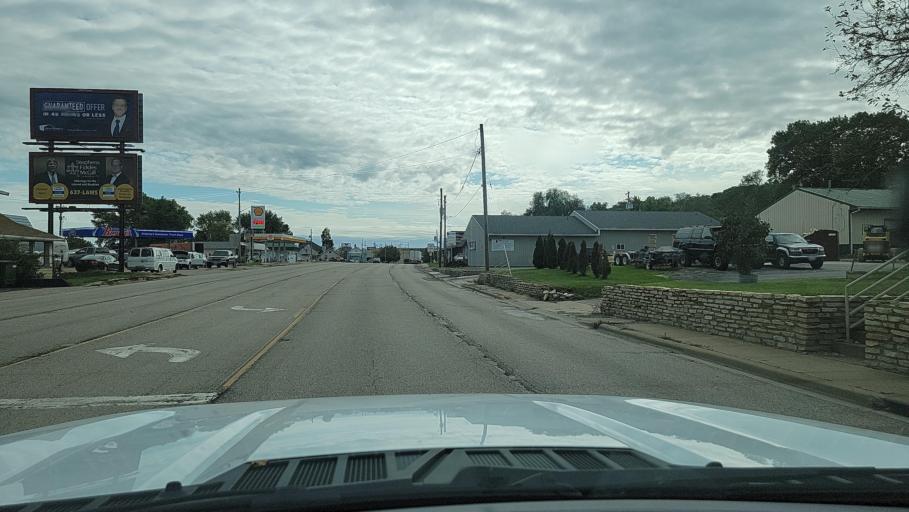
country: US
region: Illinois
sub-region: Peoria County
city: Bartonville
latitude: 40.6495
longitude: -89.6497
